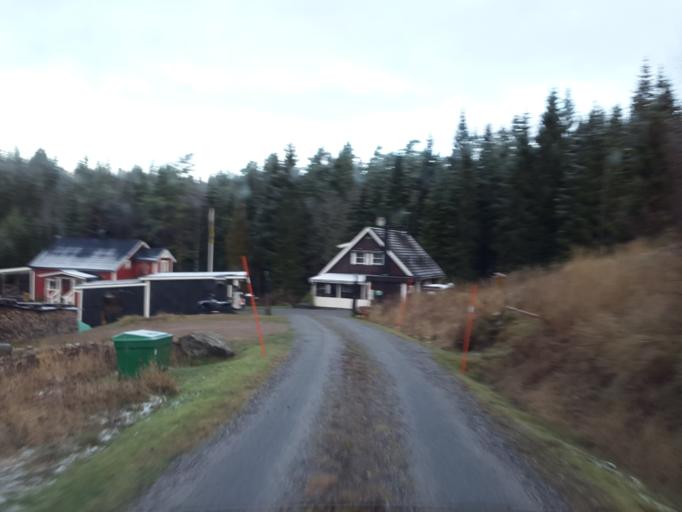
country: SE
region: Vaestra Goetaland
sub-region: Vargarda Kommun
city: Jonstorp
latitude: 57.8479
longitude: 12.6797
